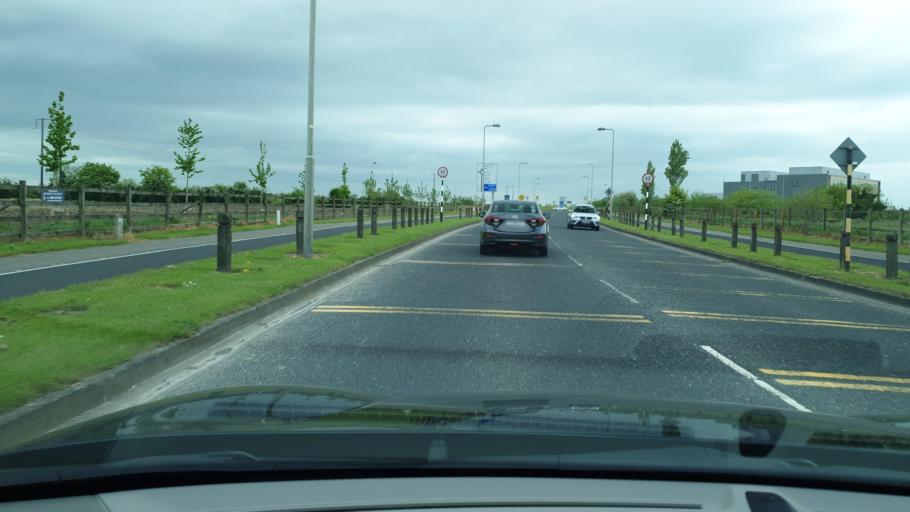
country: IE
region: Leinster
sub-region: Kildare
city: Sallins
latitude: 53.2333
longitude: -6.6782
